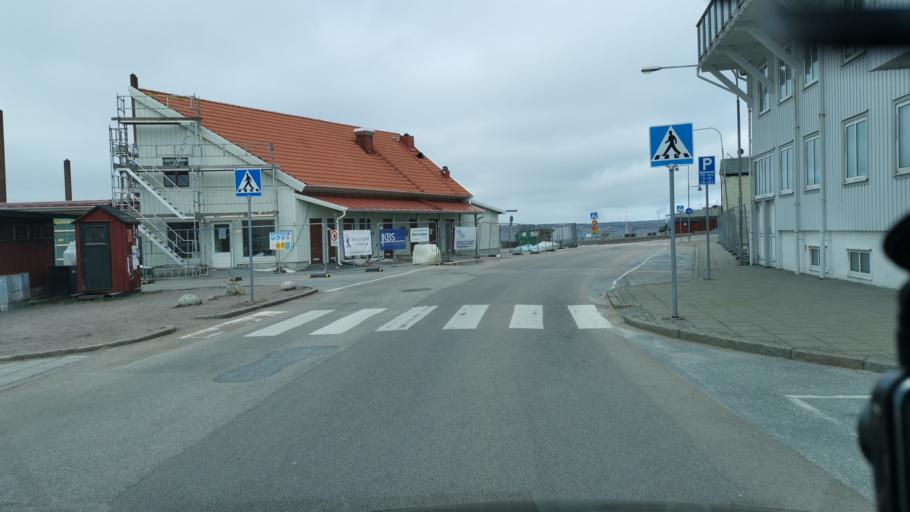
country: SE
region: Vaestra Goetaland
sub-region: Lysekils Kommun
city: Lysekil
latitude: 58.2763
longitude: 11.4251
